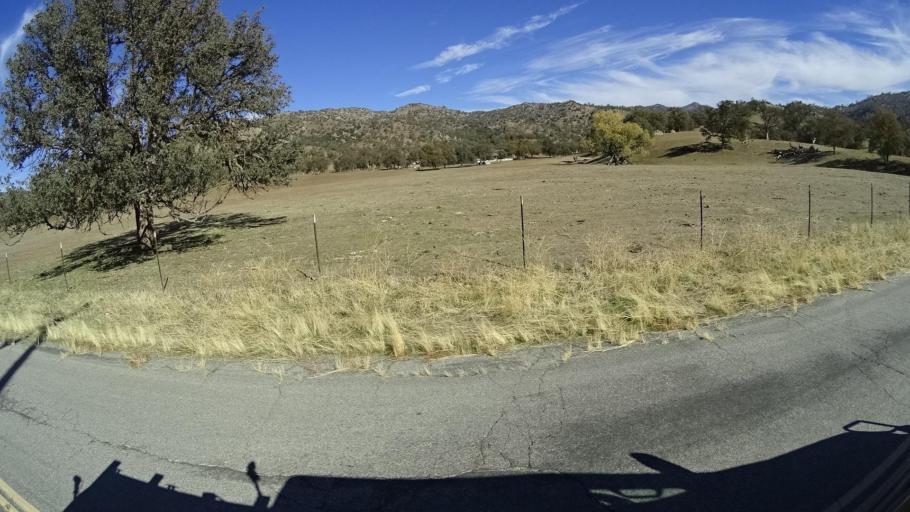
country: US
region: California
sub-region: Kern County
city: Alta Sierra
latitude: 35.6188
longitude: -118.7324
